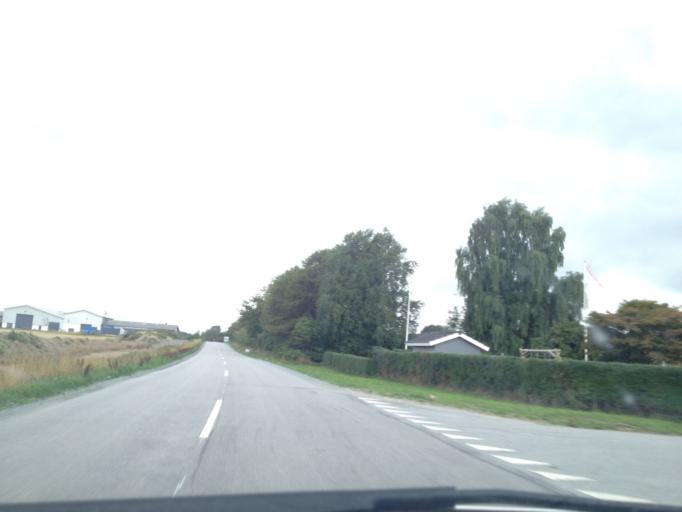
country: DK
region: South Denmark
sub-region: Kolding Kommune
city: Christiansfeld
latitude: 55.3071
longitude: 9.5055
